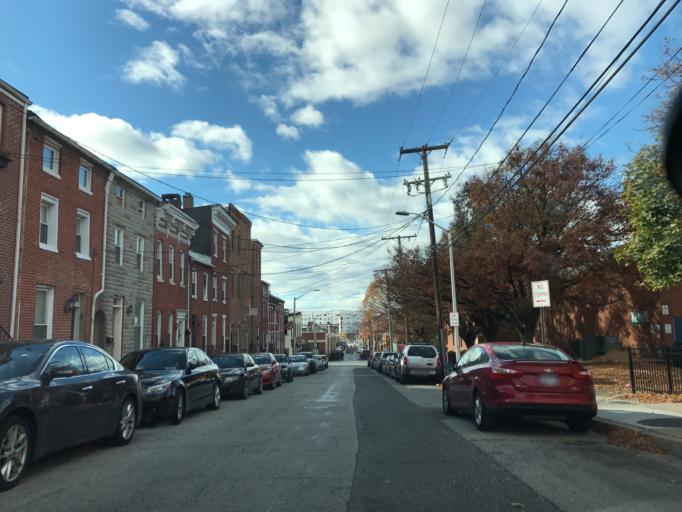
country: US
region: Maryland
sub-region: City of Baltimore
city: Baltimore
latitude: 39.2772
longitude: -76.6112
